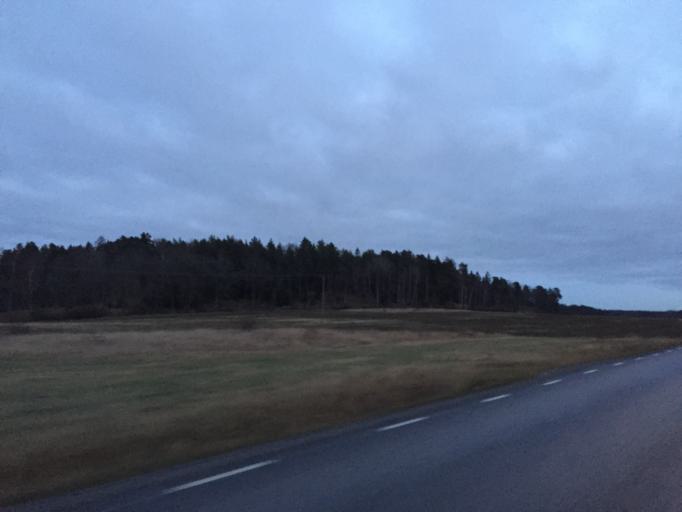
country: SE
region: Stockholm
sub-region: Salems Kommun
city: Ronninge
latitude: 59.2201
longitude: 17.7537
